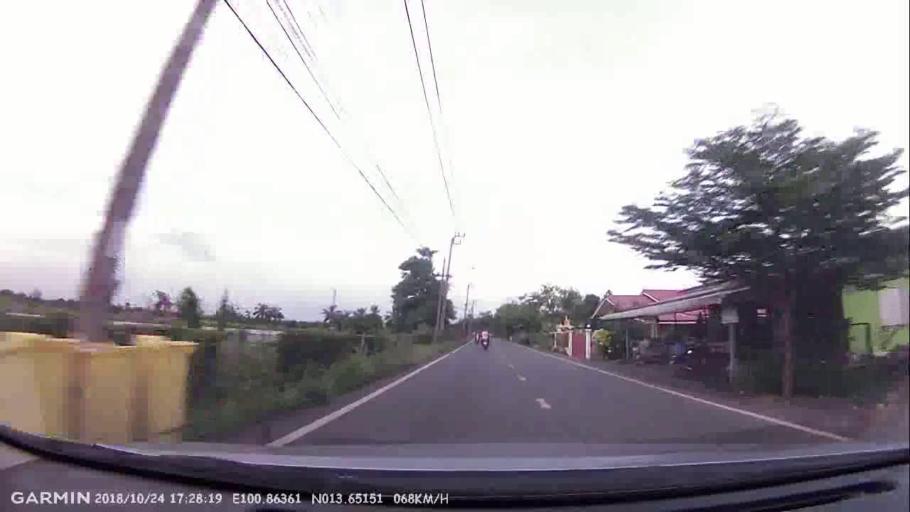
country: TH
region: Samut Prakan
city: Ban Khlong Bang Sao Thong
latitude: 13.6516
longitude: 100.8637
